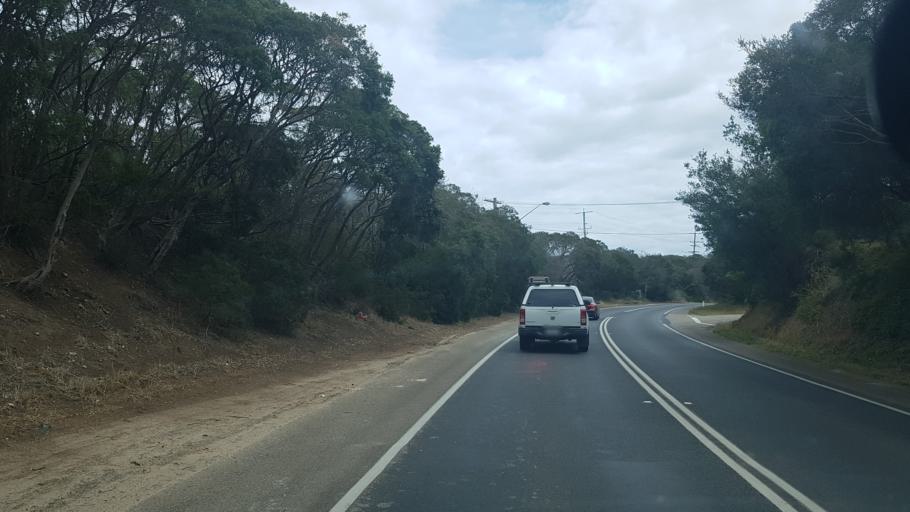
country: AU
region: Victoria
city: Rye
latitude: -38.3789
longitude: 144.8056
